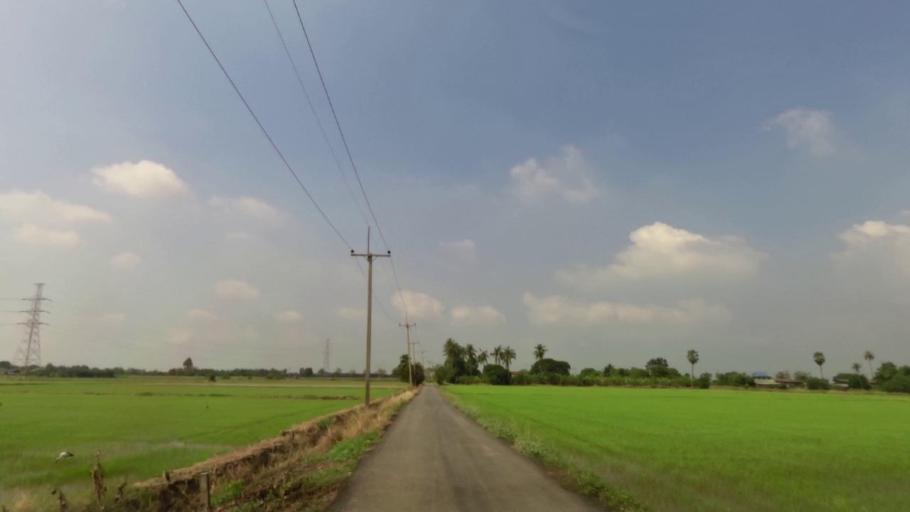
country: TH
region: Ang Thong
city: Pho Thong
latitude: 14.6197
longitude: 100.4012
